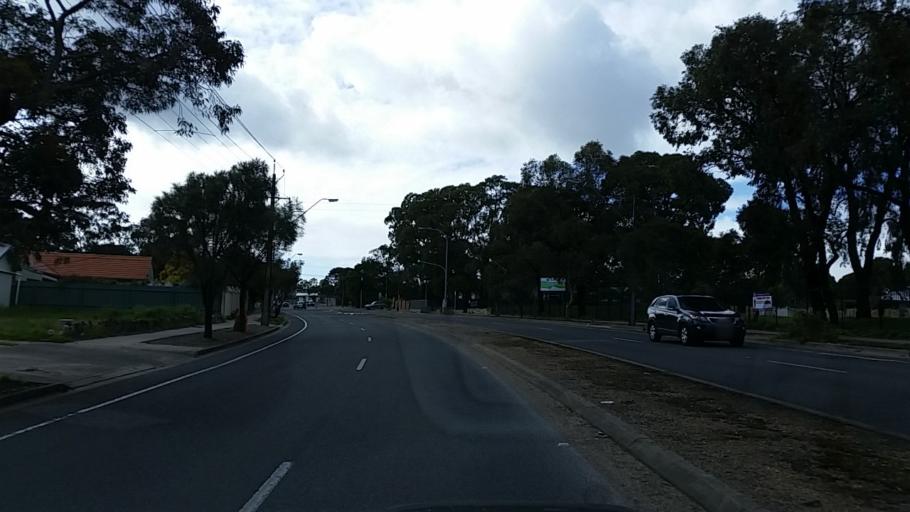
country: AU
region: South Australia
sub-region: Onkaparinga
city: Bedford Park
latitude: -35.0271
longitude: 138.5888
